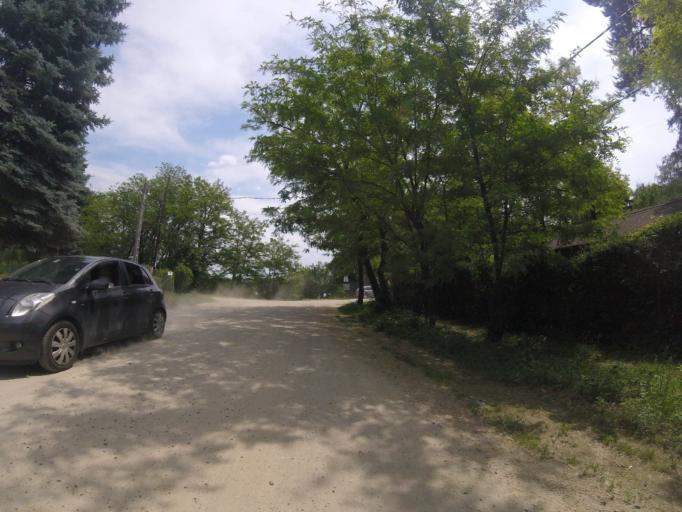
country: HU
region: Pest
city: Szodliget
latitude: 47.7153
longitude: 19.1213
